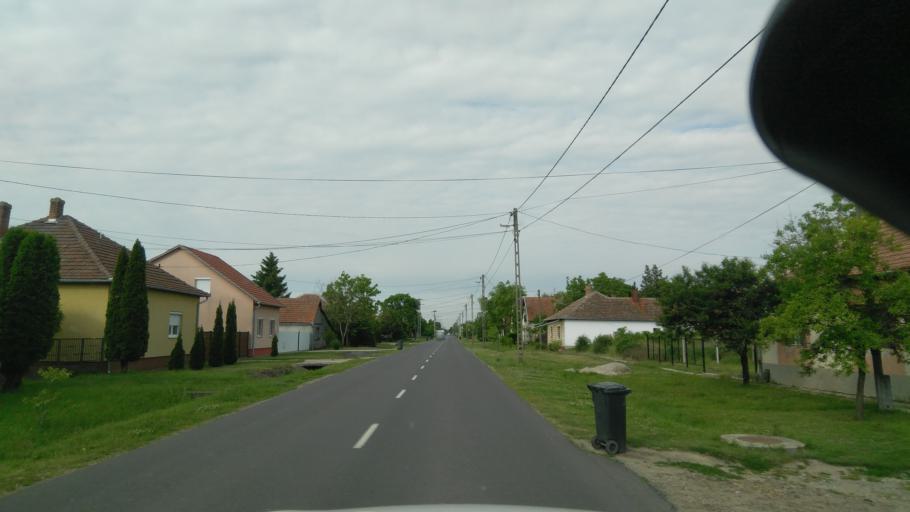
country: HU
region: Bekes
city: Ketegyhaza
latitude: 46.5476
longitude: 21.1805
